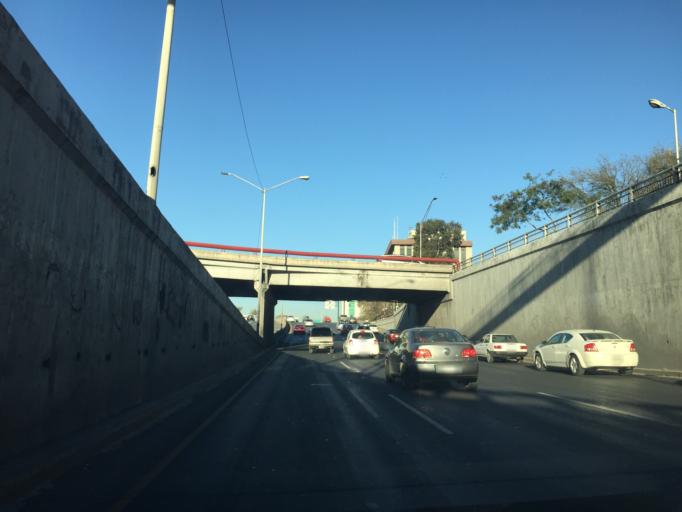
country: MX
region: Nuevo Leon
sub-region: Monterrey
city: Monterrey
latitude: 25.6656
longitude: -100.3200
